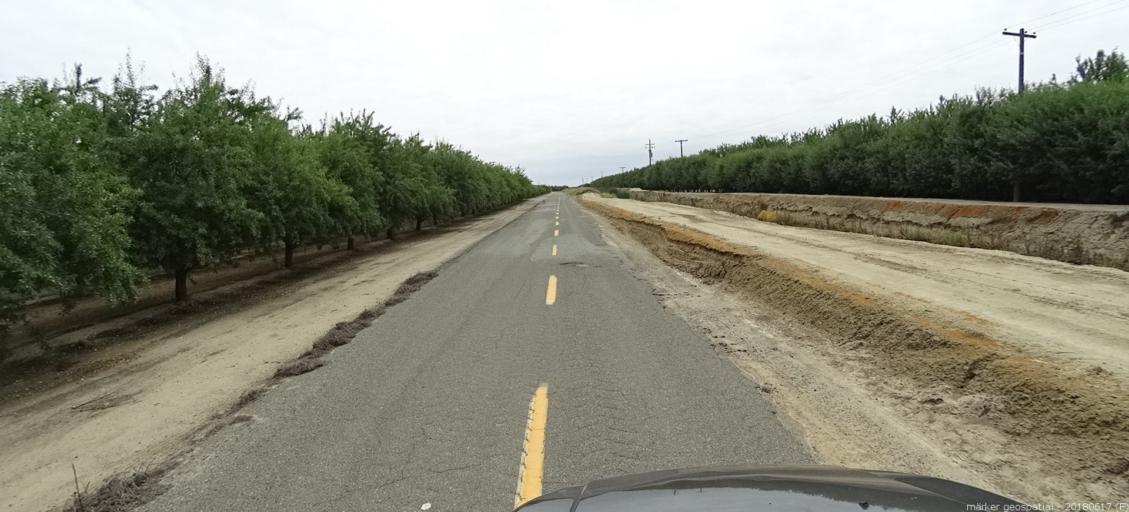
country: US
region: California
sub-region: Madera County
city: Fairmead
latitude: 36.9821
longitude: -120.2358
